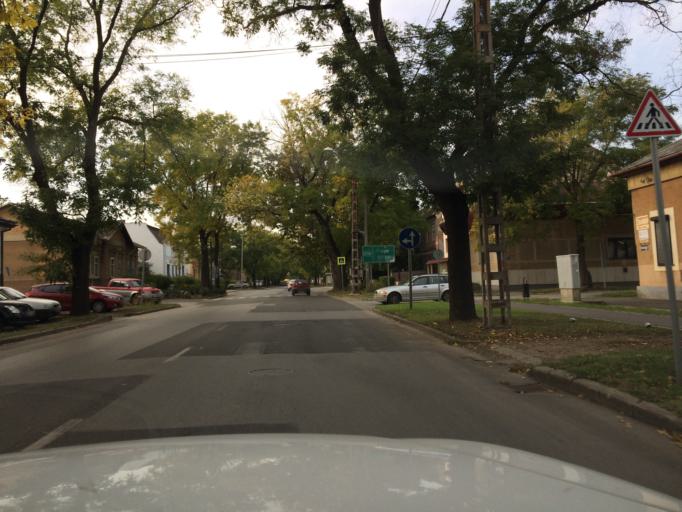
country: HU
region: Szabolcs-Szatmar-Bereg
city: Nyiregyhaza
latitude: 47.9553
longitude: 21.7099
